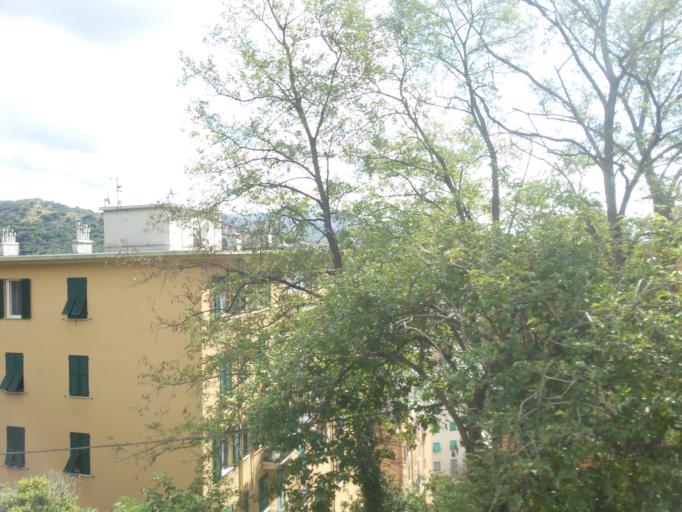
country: IT
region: Liguria
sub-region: Provincia di Genova
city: Genoa
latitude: 44.4237
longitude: 8.9435
